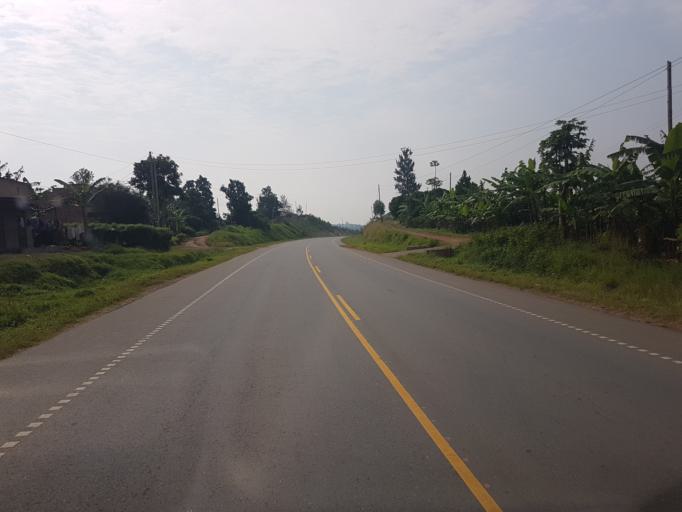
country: UG
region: Western Region
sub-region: Sheema District
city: Kibingo
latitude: -0.6348
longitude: 30.5366
